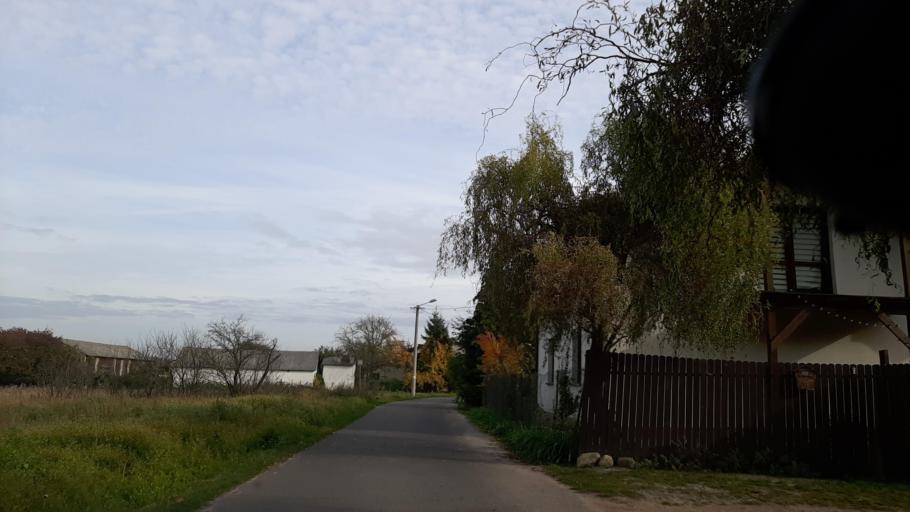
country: PL
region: Lublin Voivodeship
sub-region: Powiat lubelski
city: Garbow
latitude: 51.4106
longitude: 22.3833
